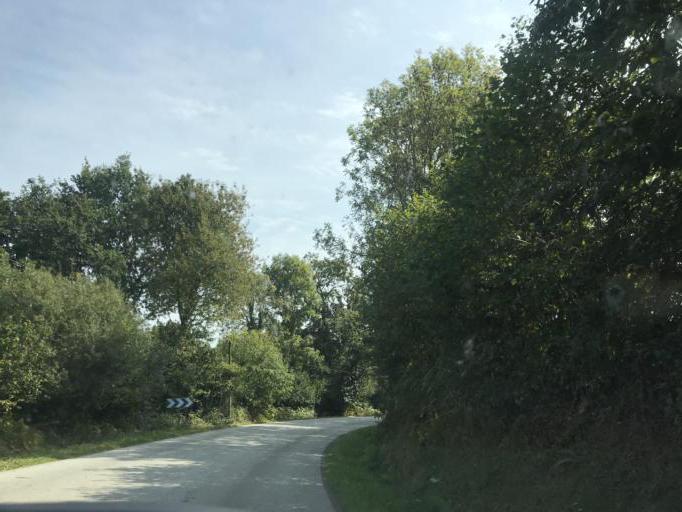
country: FR
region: Brittany
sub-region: Departement du Finistere
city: Loperec
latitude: 48.3010
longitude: -4.0206
